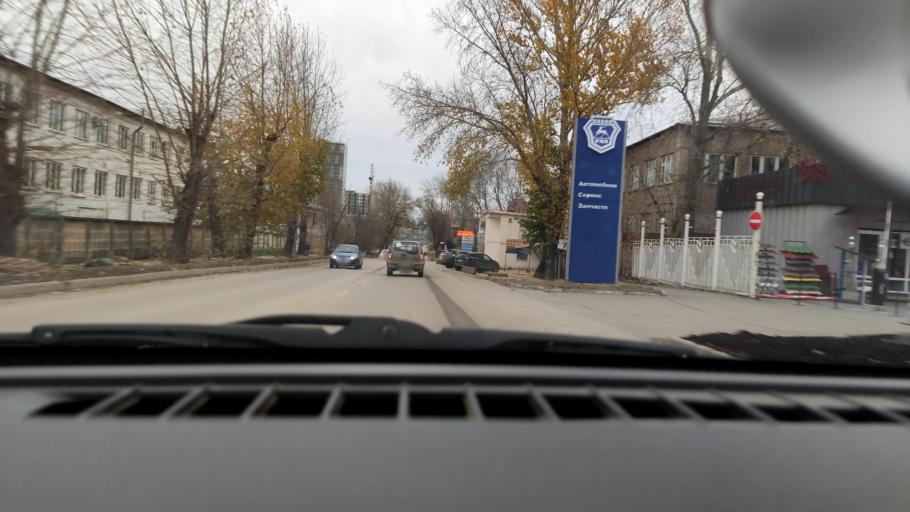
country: RU
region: Perm
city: Kondratovo
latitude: 57.9702
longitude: 56.1795
